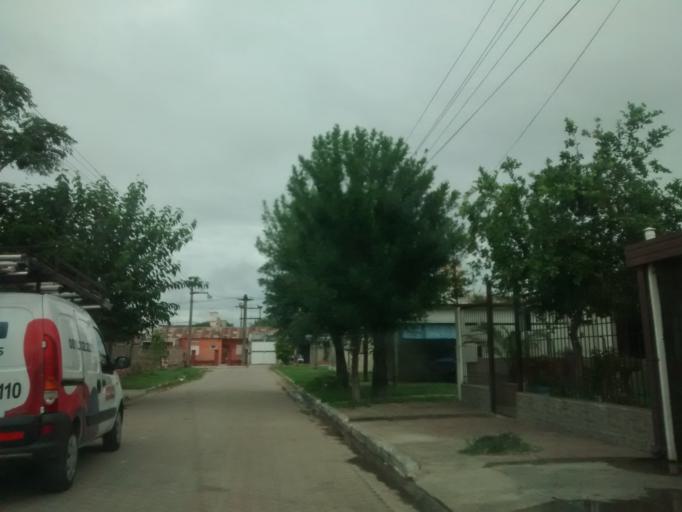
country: AR
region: Chaco
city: Puerto Tirol
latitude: -27.3719
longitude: -59.0989
